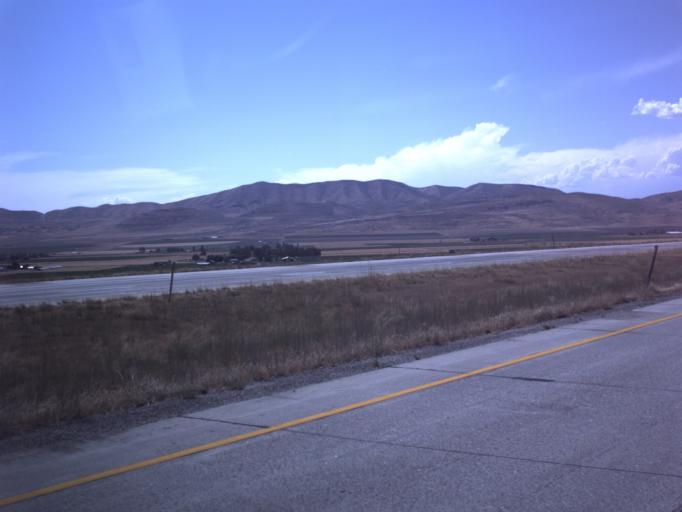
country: US
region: Utah
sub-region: Box Elder County
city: Tremonton
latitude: 41.7258
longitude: -112.2395
